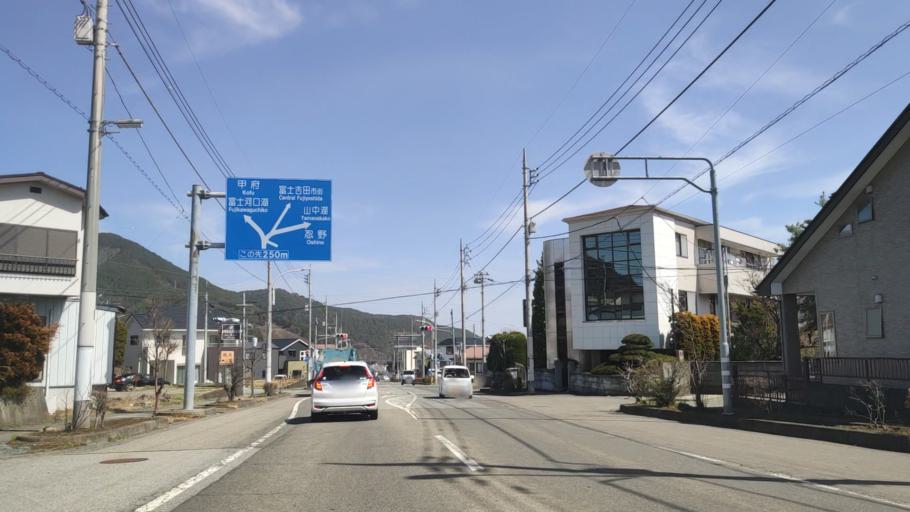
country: JP
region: Yamanashi
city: Fujikawaguchiko
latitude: 35.4890
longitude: 138.7911
